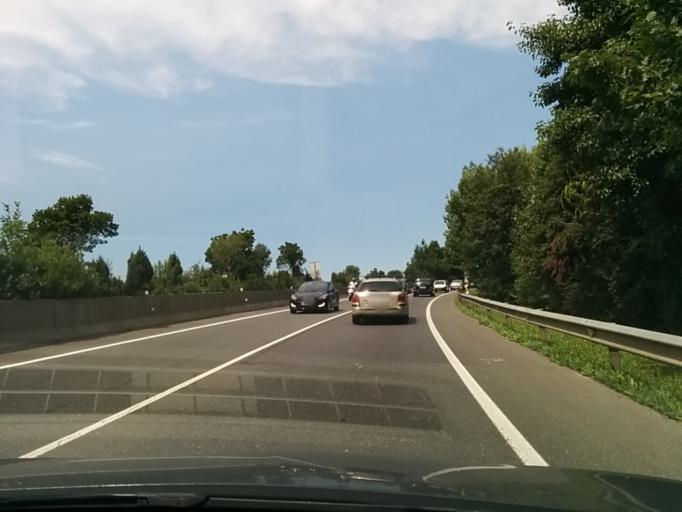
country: ES
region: Basque Country
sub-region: Provincia de Guipuzcoa
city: Lezo
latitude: 43.3112
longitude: -1.8892
